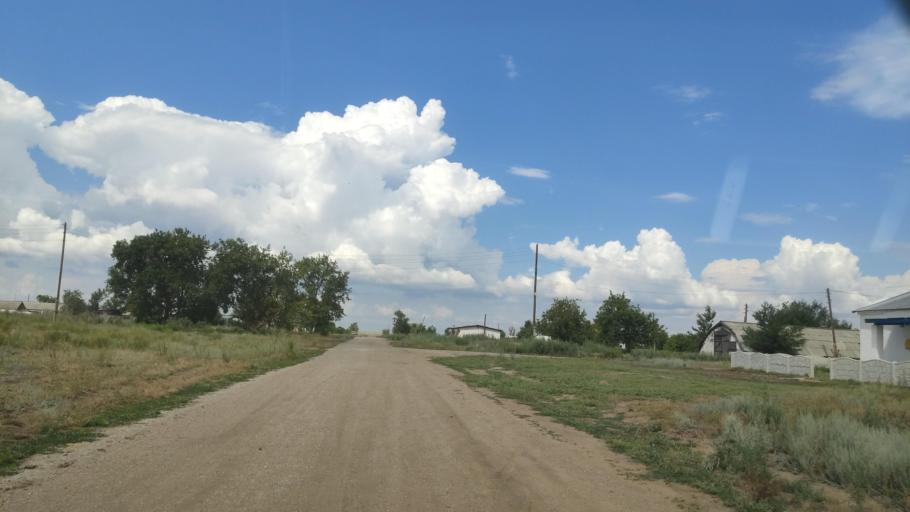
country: KZ
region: Pavlodar
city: Pavlodar
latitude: 52.6189
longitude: 77.2070
